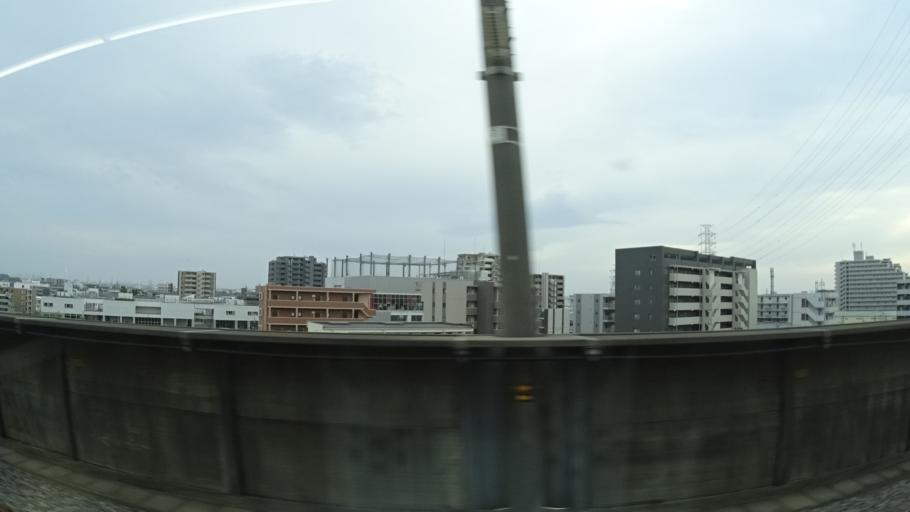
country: JP
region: Saitama
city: Shimotoda
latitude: 35.8266
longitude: 139.6615
